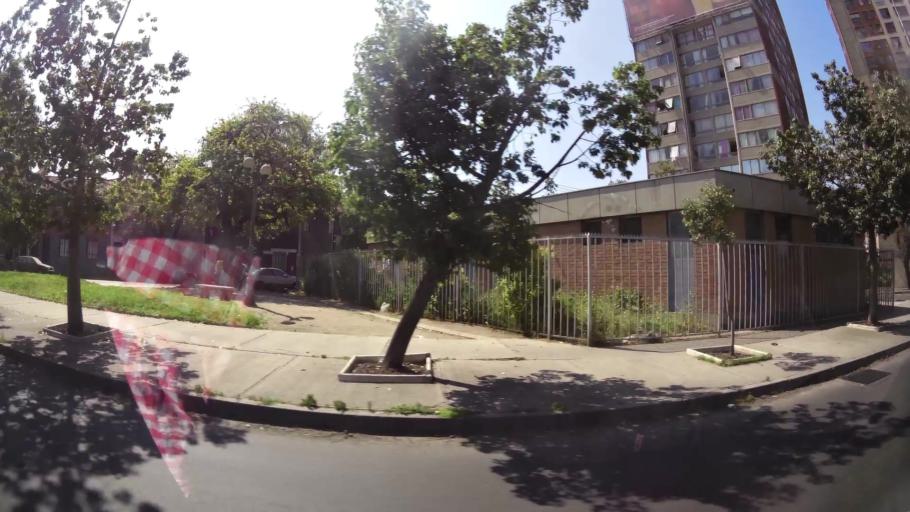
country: CL
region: Santiago Metropolitan
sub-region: Provincia de Santiago
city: Santiago
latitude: -33.4294
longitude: -70.6585
